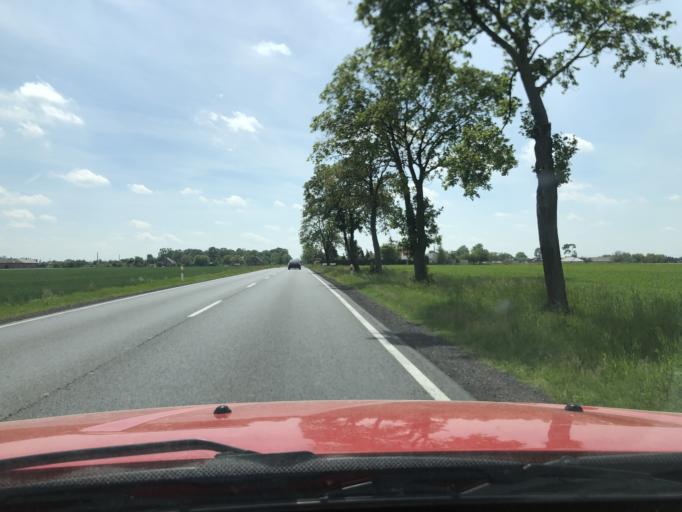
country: PL
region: Greater Poland Voivodeship
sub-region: Kalisz
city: Kalisz
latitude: 51.8203
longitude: 18.0936
